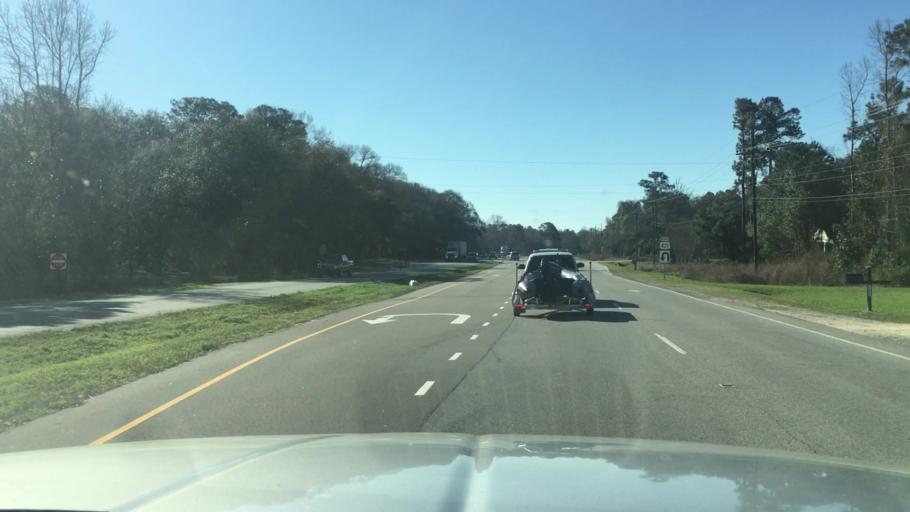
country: US
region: North Carolina
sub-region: New Hanover County
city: Sea Breeze
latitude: 34.0824
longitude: -77.8952
